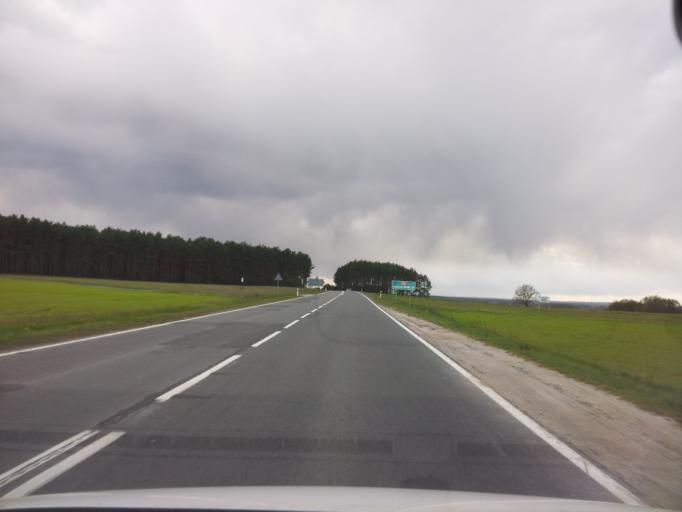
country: PL
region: Lubusz
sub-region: Powiat krosnienski
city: Dabie
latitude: 52.0185
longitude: 15.1253
